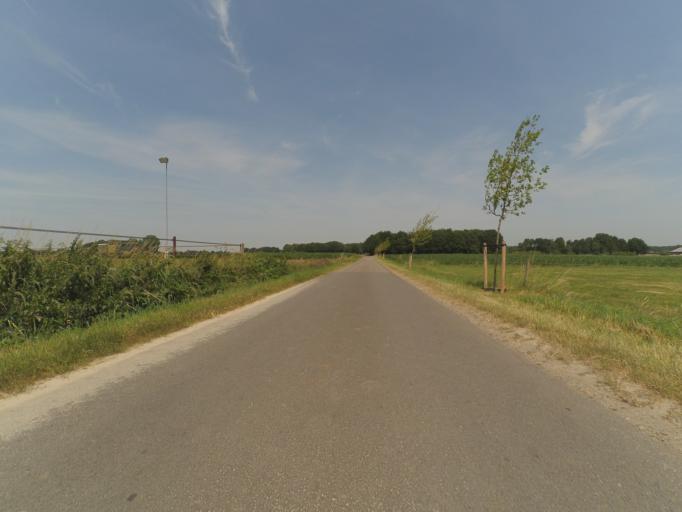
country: BE
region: Flanders
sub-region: Provincie Antwerpen
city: Essen
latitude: 51.4499
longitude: 4.3934
